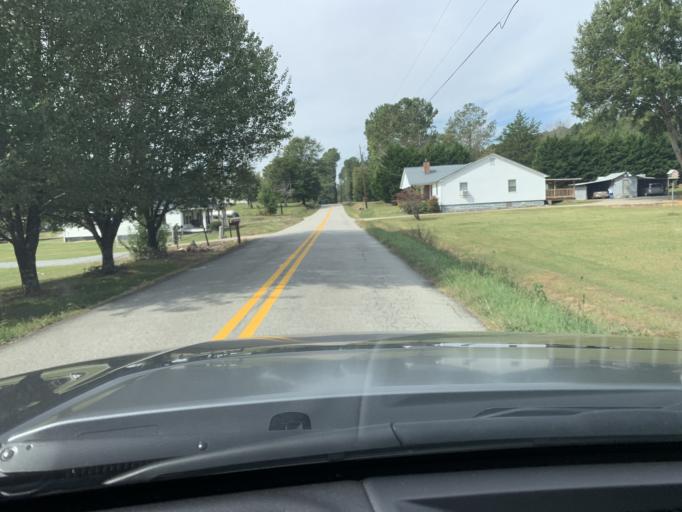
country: US
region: Georgia
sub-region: Polk County
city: Cedartown
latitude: 33.9742
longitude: -85.2775
